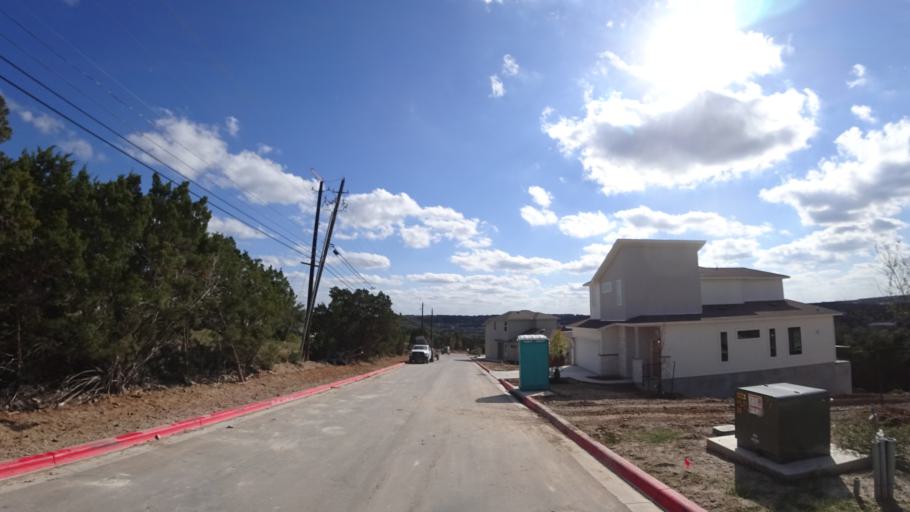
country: US
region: Texas
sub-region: Travis County
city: Barton Creek
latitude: 30.2429
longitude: -97.8765
